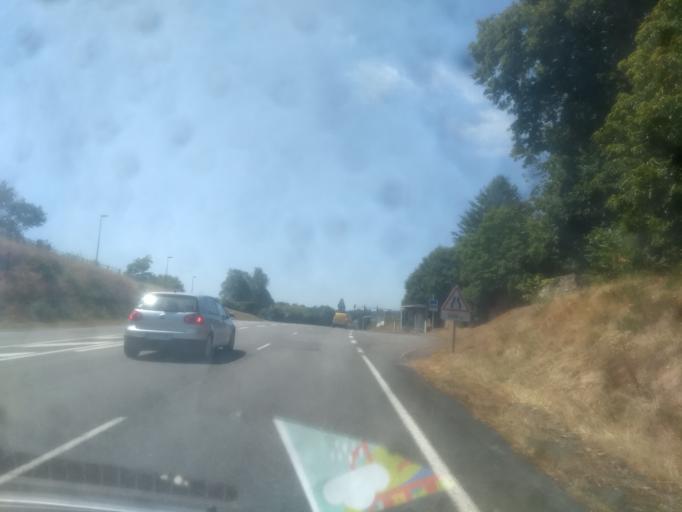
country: FR
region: Limousin
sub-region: Departement de la Haute-Vienne
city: Bessines-sur-Gartempe
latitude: 46.1079
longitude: 1.3710
